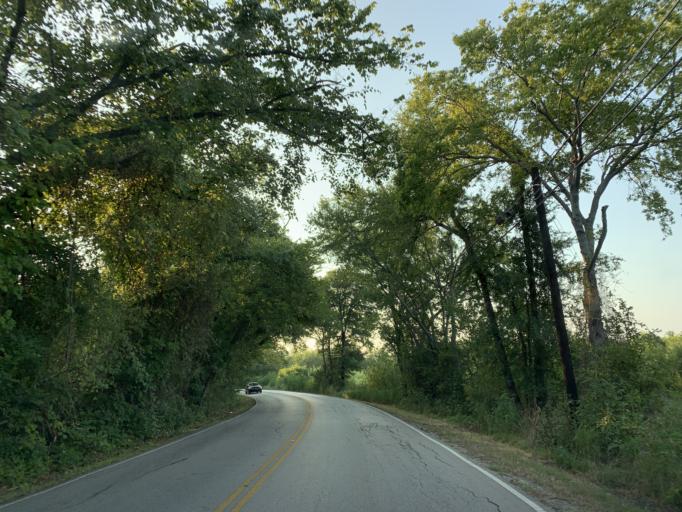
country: US
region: Texas
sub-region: Tarrant County
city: Hurst
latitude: 32.7784
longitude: -97.1752
